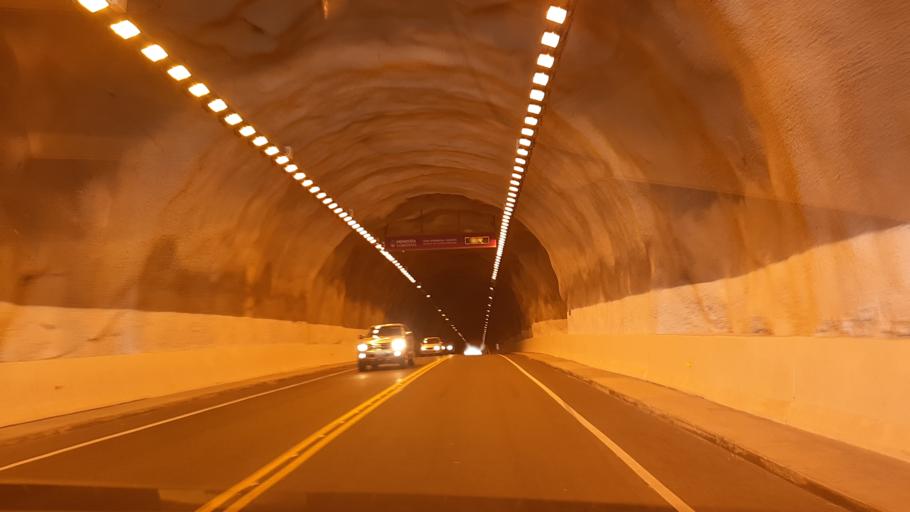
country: AR
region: Mendoza
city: Lujan de Cuyo
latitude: -32.9973
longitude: -69.1373
